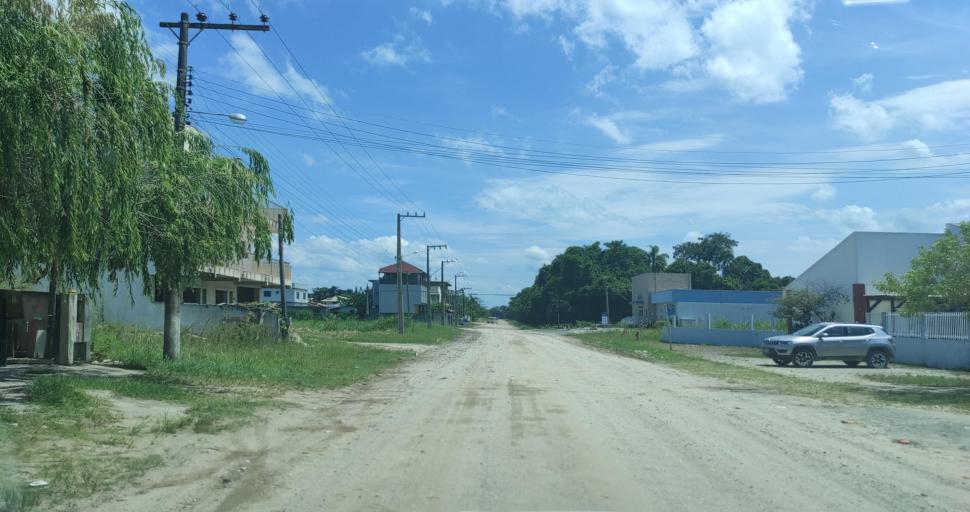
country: BR
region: Santa Catarina
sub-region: Porto Belo
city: Porto Belo
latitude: -27.1773
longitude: -48.5073
